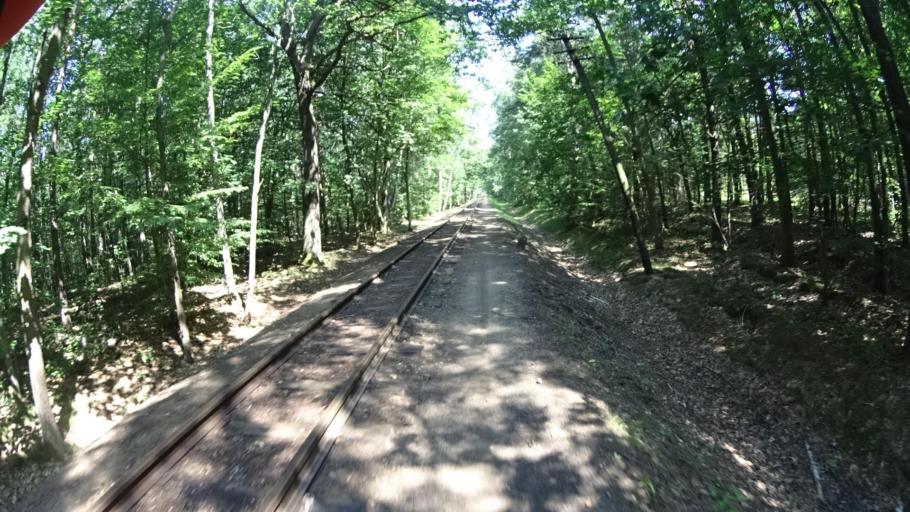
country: PL
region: Masovian Voivodeship
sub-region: Powiat piaseczynski
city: Prazmow
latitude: 52.0122
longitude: 20.9234
